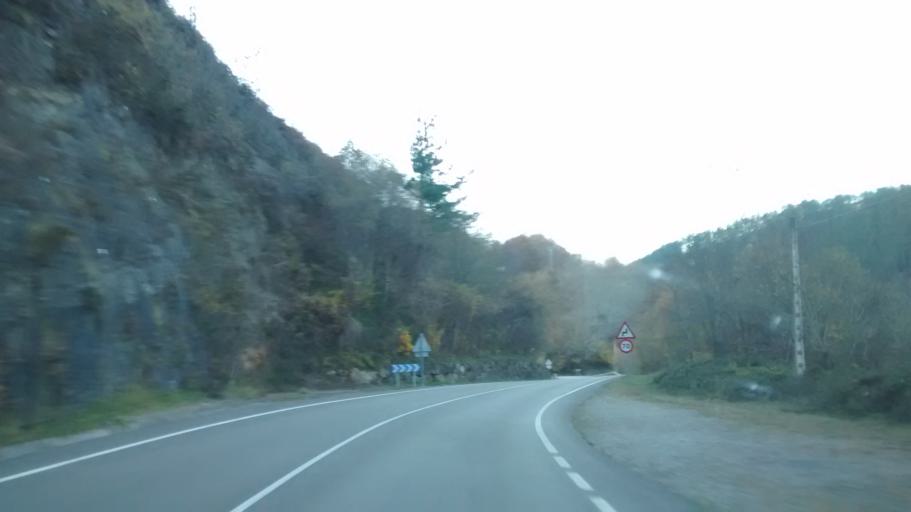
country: ES
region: Cantabria
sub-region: Provincia de Cantabria
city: Ruente
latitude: 43.1748
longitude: -4.2985
